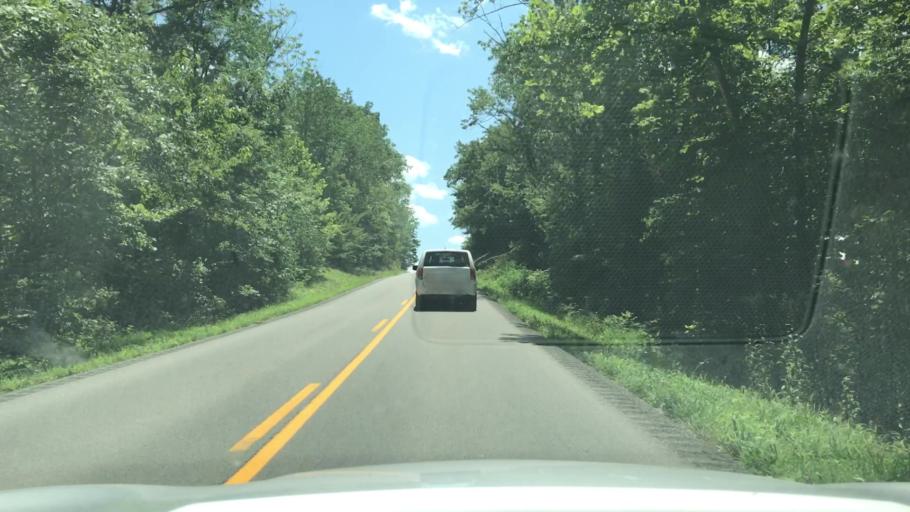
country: US
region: Kentucky
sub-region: Christian County
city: Hopkinsville
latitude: 36.9065
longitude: -87.4457
